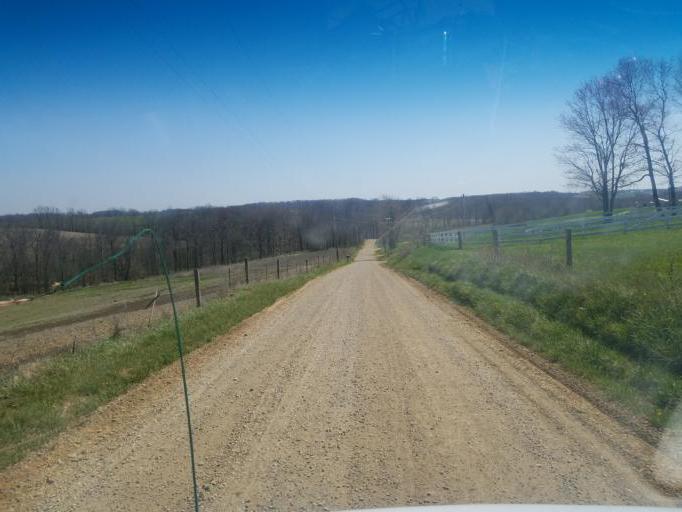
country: US
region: Ohio
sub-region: Knox County
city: Oak Hill
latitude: 40.3335
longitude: -82.1909
